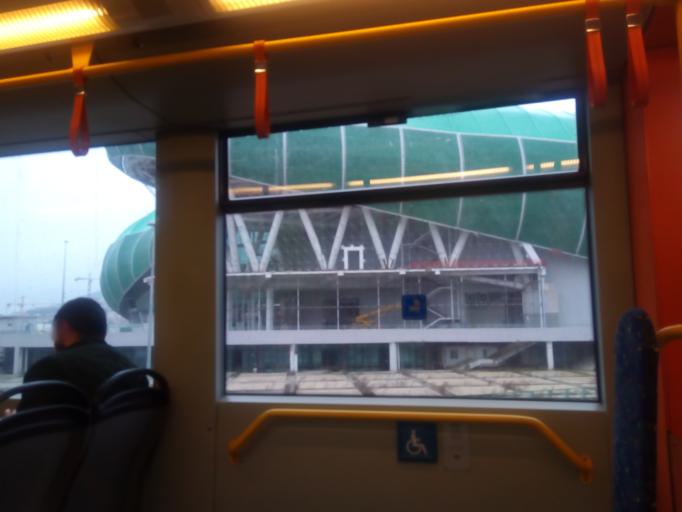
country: TR
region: Bursa
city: Yildirim
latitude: 40.2128
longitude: 29.0090
